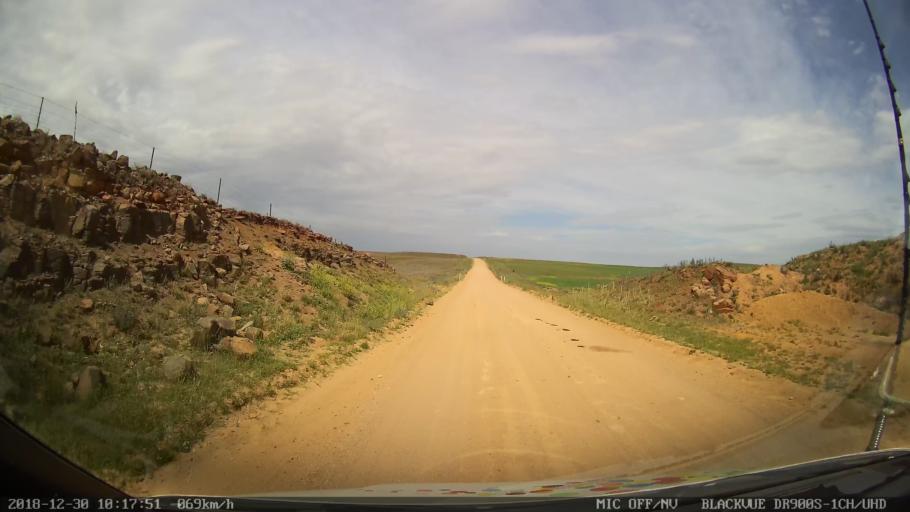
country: AU
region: New South Wales
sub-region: Snowy River
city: Berridale
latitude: -36.5498
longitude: 149.0159
